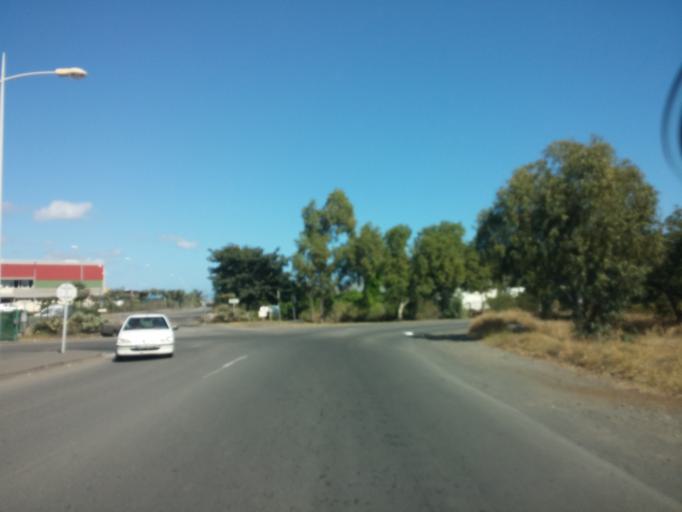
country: RE
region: Reunion
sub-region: Reunion
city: Le Port
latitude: -20.9516
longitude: 55.3010
